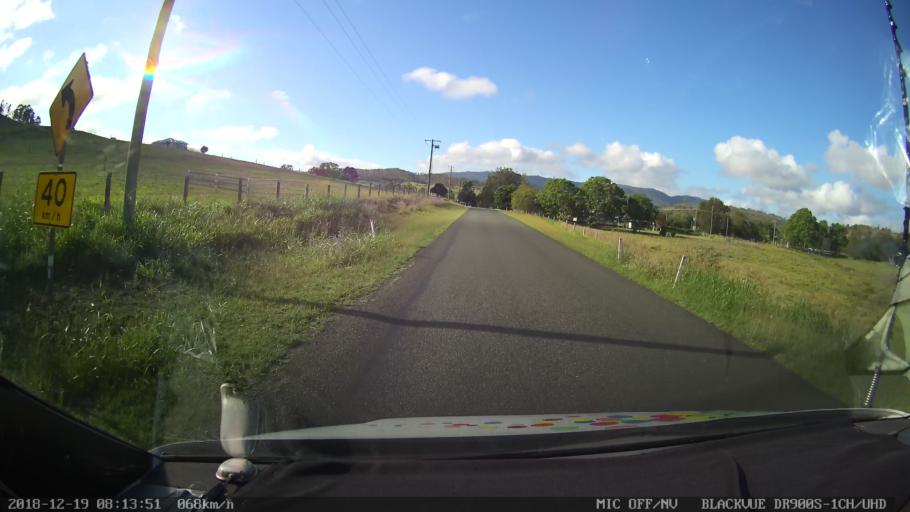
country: AU
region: Queensland
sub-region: Logan
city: Cedar Vale
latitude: -28.2429
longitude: 152.8901
